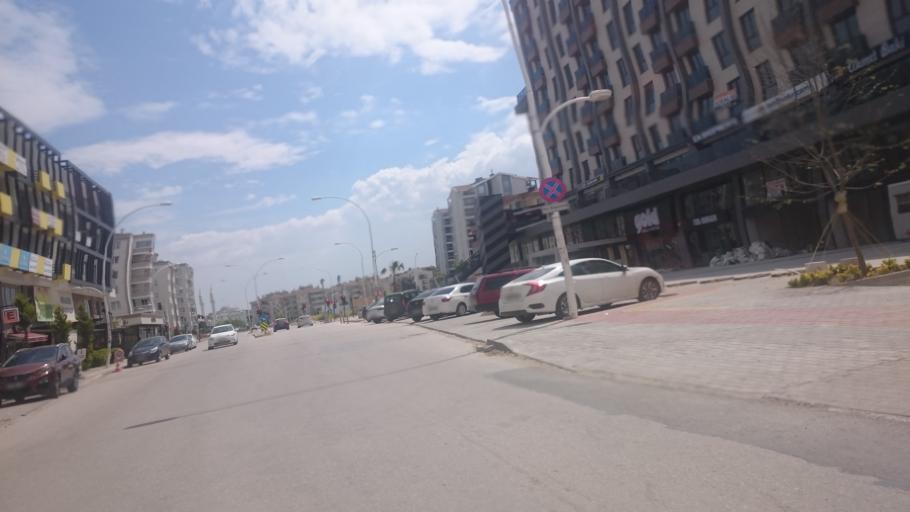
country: TR
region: Bursa
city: Cali
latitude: 40.2254
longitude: 28.9136
